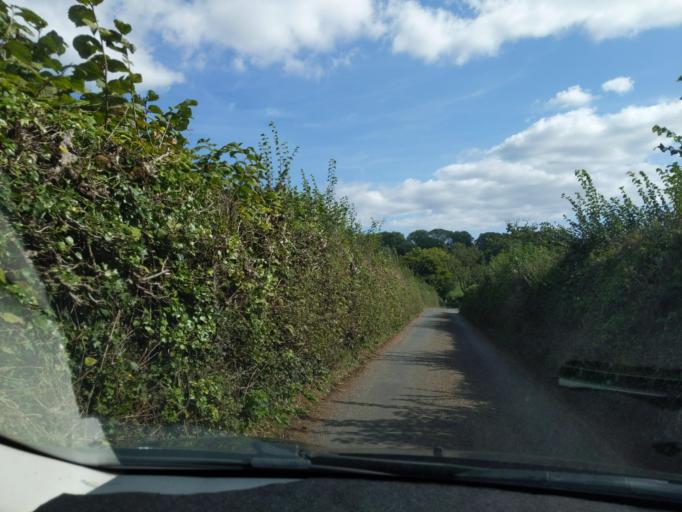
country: GB
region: England
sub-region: Devon
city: Marldon
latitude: 50.4605
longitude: -3.6163
